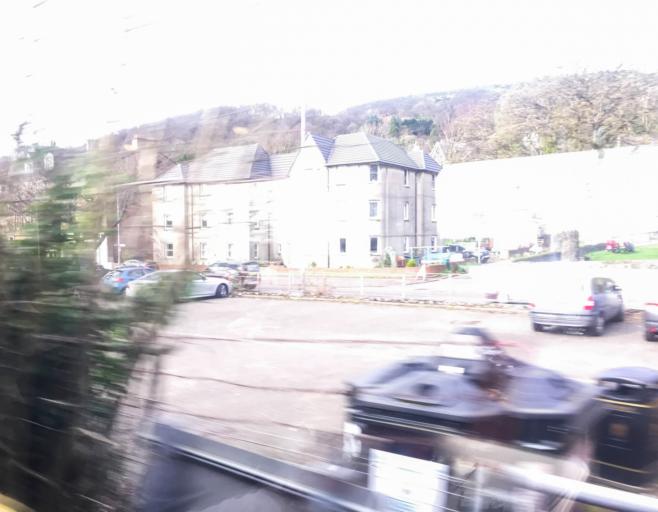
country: GB
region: Scotland
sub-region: Renfrewshire
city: Bishopton
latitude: 55.9306
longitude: -4.4853
